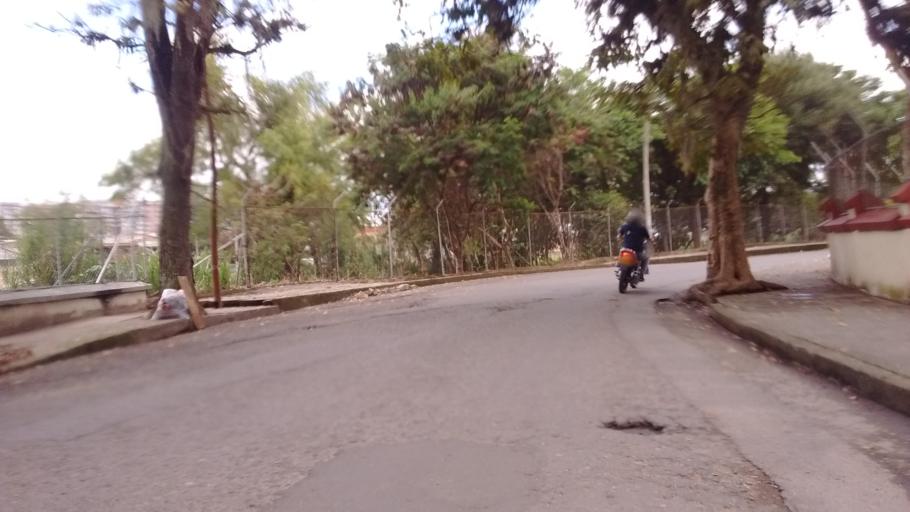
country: CO
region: Cauca
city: Popayan
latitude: 2.4472
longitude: -76.6010
